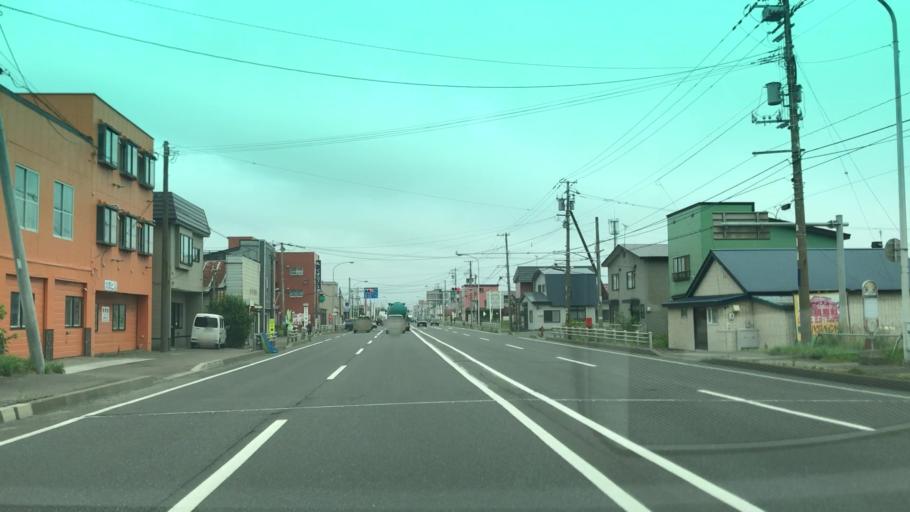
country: JP
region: Hokkaido
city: Muroran
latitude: 42.3558
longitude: 141.0493
